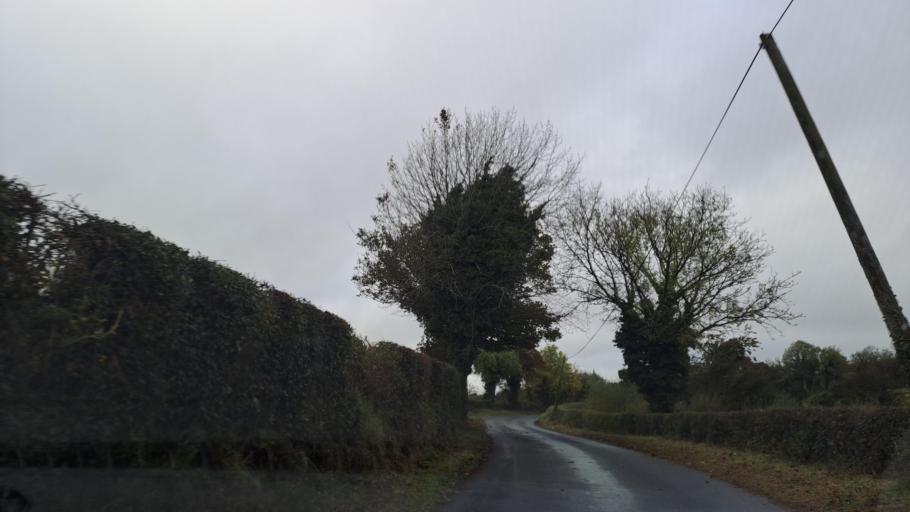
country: IE
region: Ulster
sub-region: An Cabhan
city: Bailieborough
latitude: 53.9944
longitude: -6.9465
